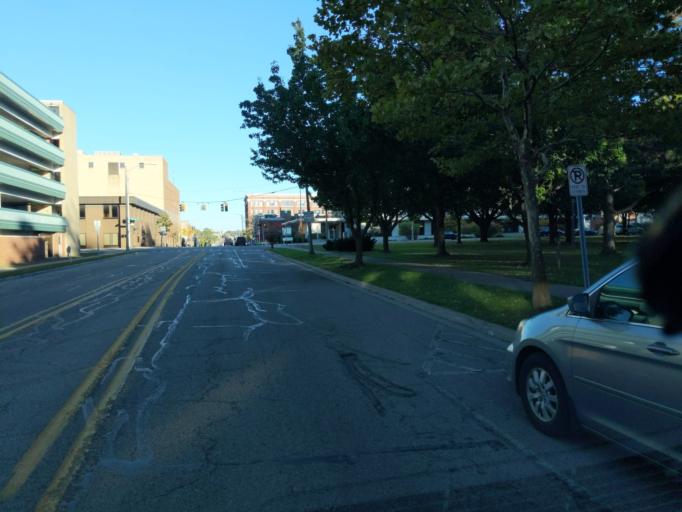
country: US
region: Michigan
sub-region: Ingham County
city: Lansing
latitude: 42.7299
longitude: -84.5549
